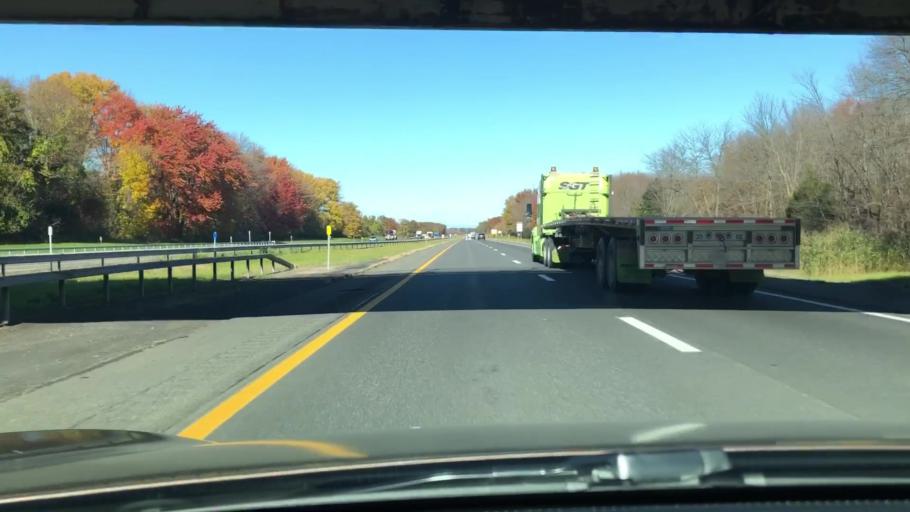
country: US
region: New York
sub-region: Ulster County
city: Glasco
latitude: 42.0394
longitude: -73.9892
